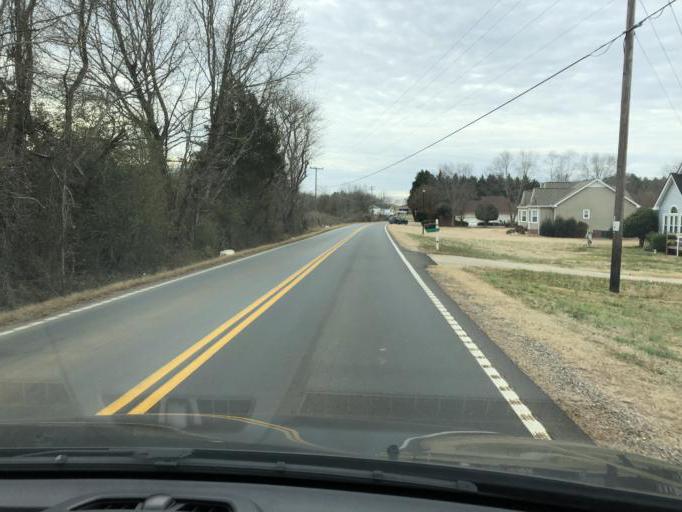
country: US
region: South Carolina
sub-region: Greenville County
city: Five Forks
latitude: 34.8688
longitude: -82.1991
